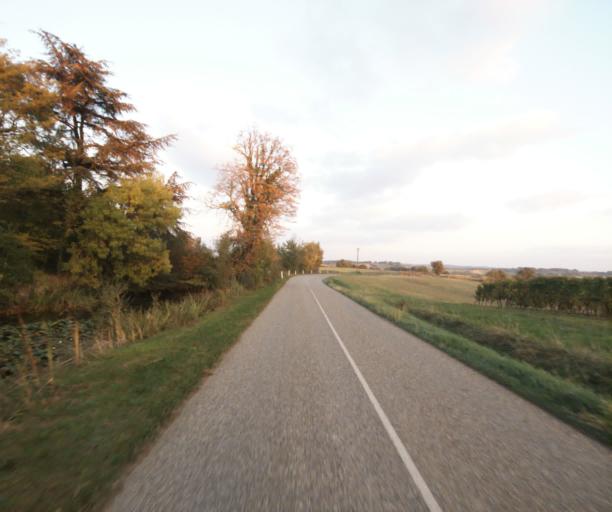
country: FR
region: Midi-Pyrenees
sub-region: Departement du Gers
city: Vic-Fezensac
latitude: 43.7972
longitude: 0.2436
